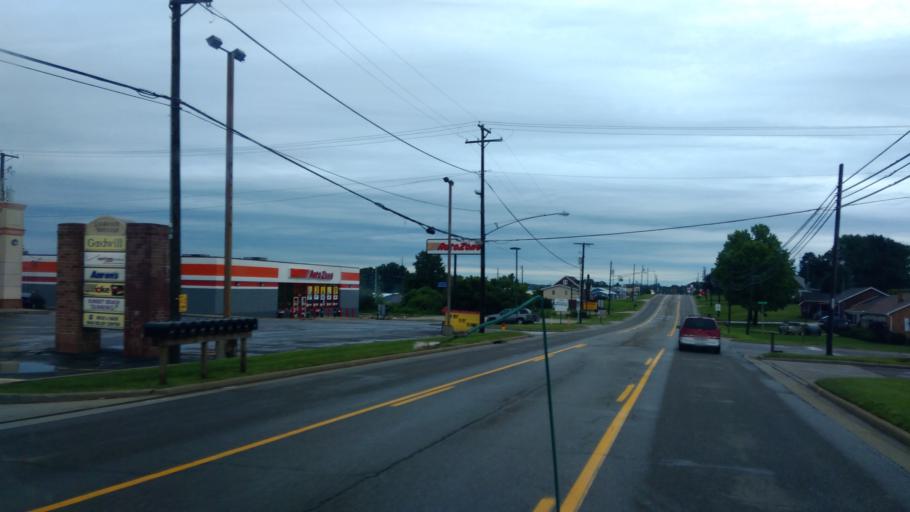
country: US
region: Ohio
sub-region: Carroll County
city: Carrollton
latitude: 40.5823
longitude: -81.0923
